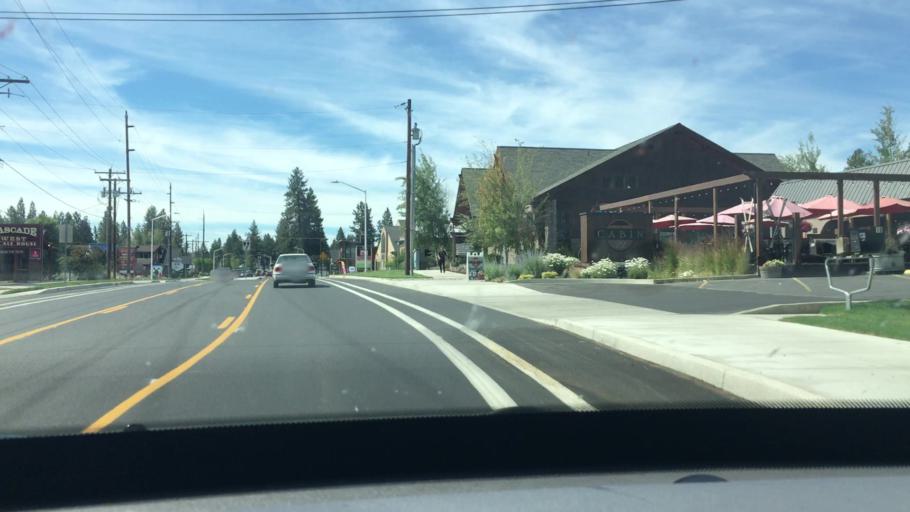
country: US
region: Oregon
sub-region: Deschutes County
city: Bend
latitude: 44.0512
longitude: -121.3319
